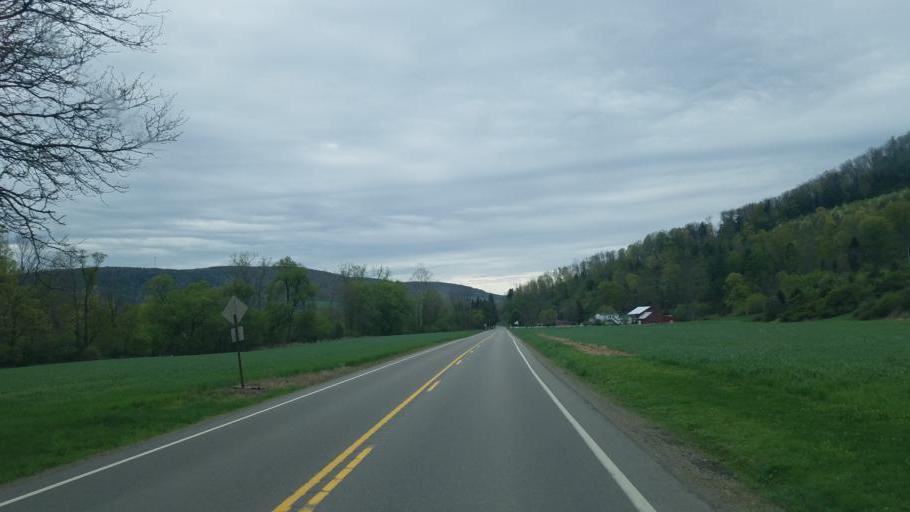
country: US
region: Pennsylvania
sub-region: Tioga County
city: Westfield
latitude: 41.9651
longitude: -77.4463
